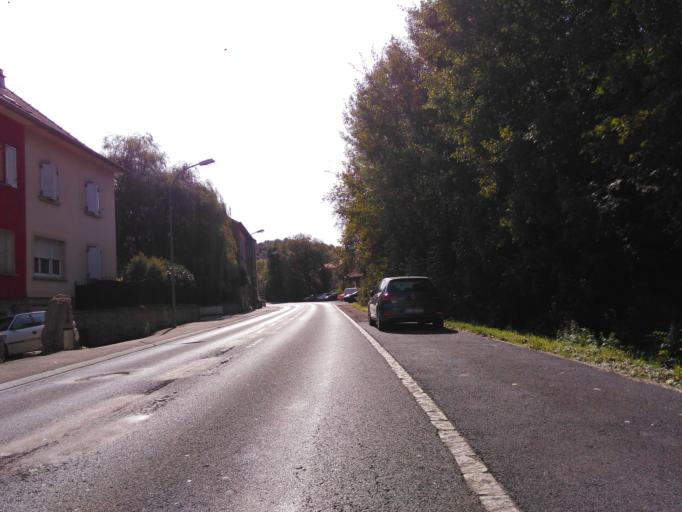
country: FR
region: Lorraine
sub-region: Departement de la Moselle
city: Ottange
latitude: 49.4473
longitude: 6.0242
